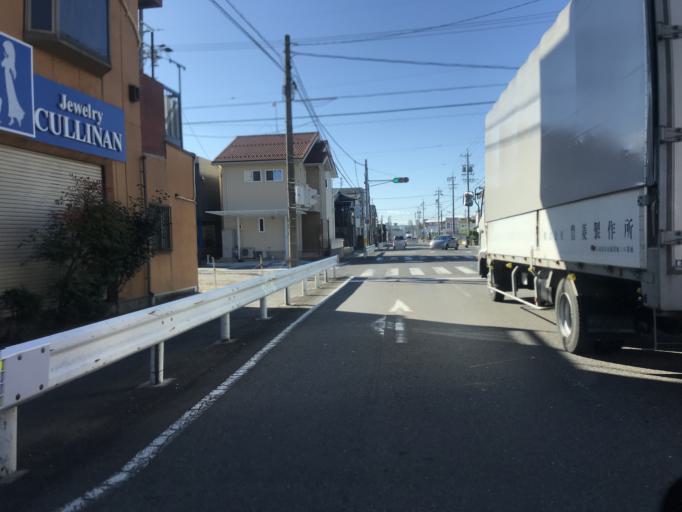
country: JP
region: Aichi
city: Nagoya-shi
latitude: 35.2031
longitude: 136.8679
